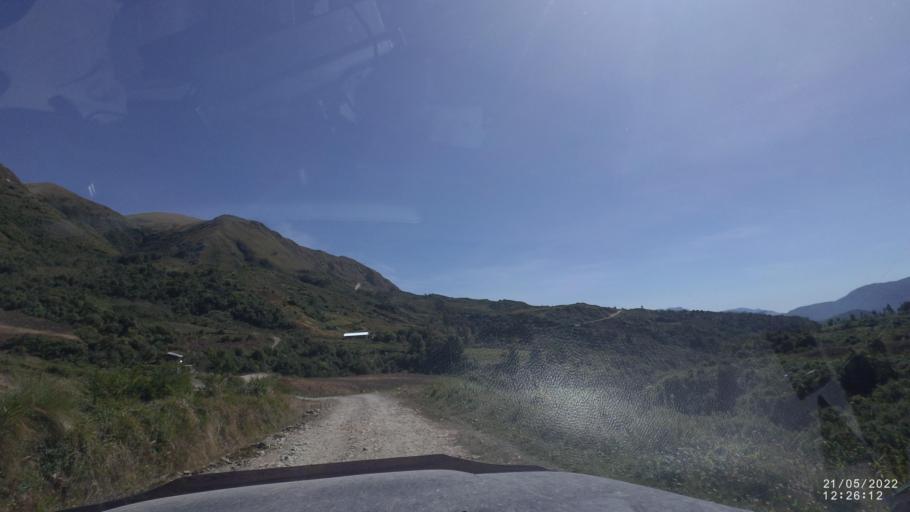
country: BO
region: Cochabamba
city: Colomi
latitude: -17.2195
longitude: -65.9094
